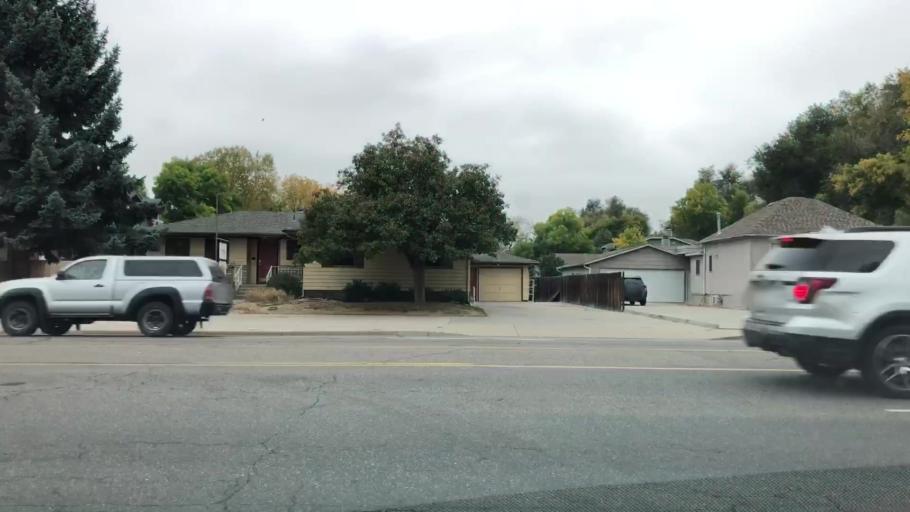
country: US
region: Colorado
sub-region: Larimer County
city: Fort Collins
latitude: 40.5661
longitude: -105.0578
